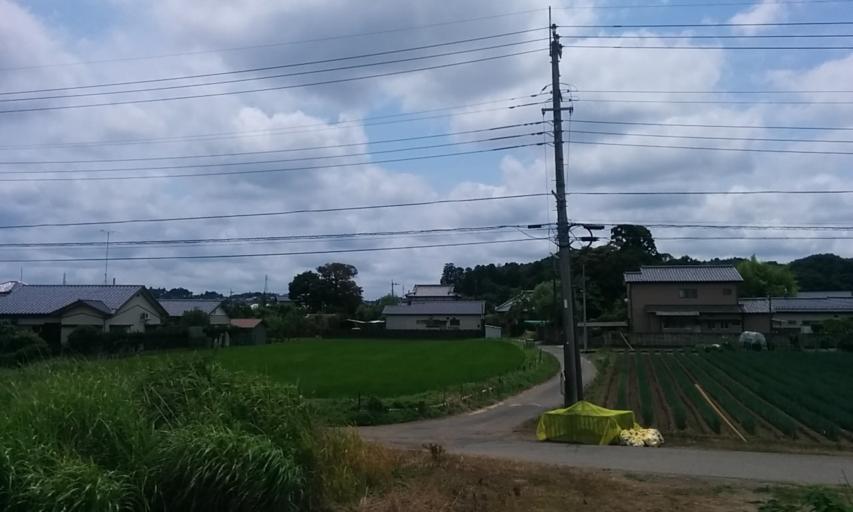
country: JP
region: Chiba
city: Katori-shi
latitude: 35.8987
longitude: 140.4756
